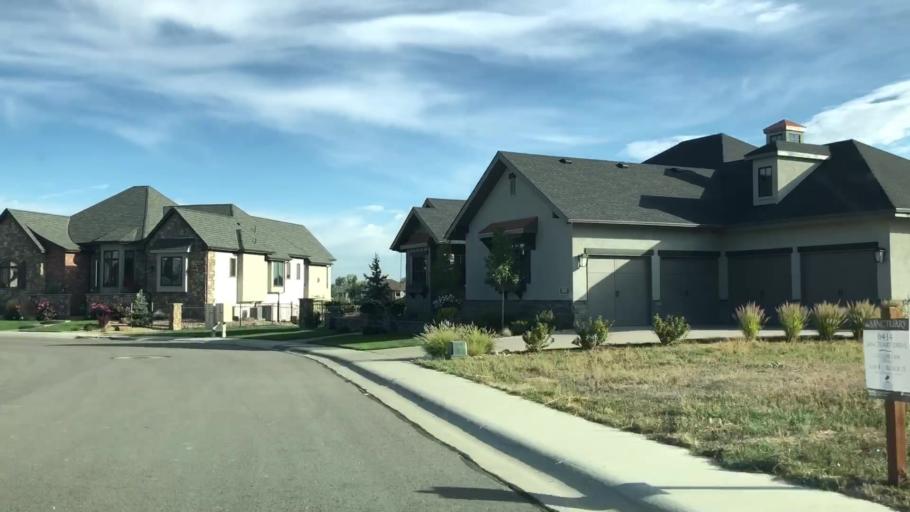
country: US
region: Colorado
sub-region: Weld County
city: Windsor
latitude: 40.4587
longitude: -104.9692
